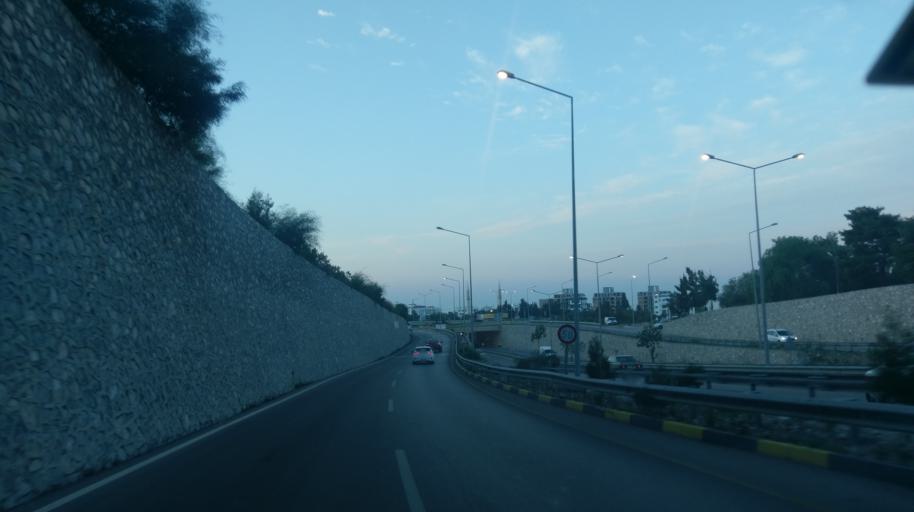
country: CY
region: Keryneia
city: Kyrenia
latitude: 35.3231
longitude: 33.3182
